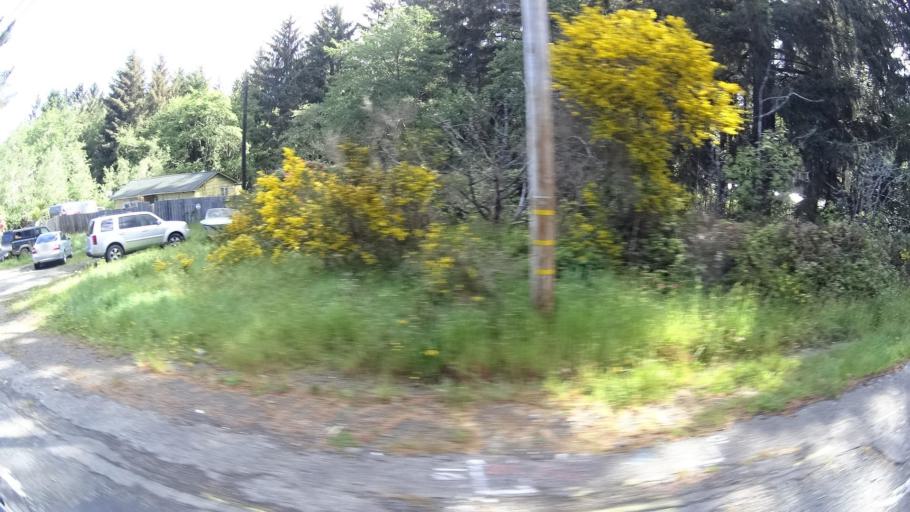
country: US
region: California
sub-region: Humboldt County
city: McKinleyville
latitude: 40.9853
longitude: -124.1055
